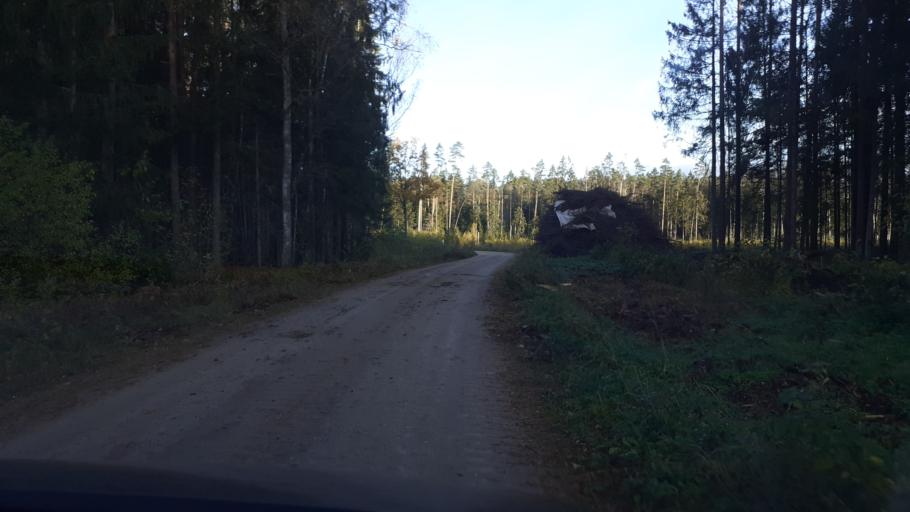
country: LV
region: Skrunda
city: Skrunda
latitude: 56.8509
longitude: 22.1076
